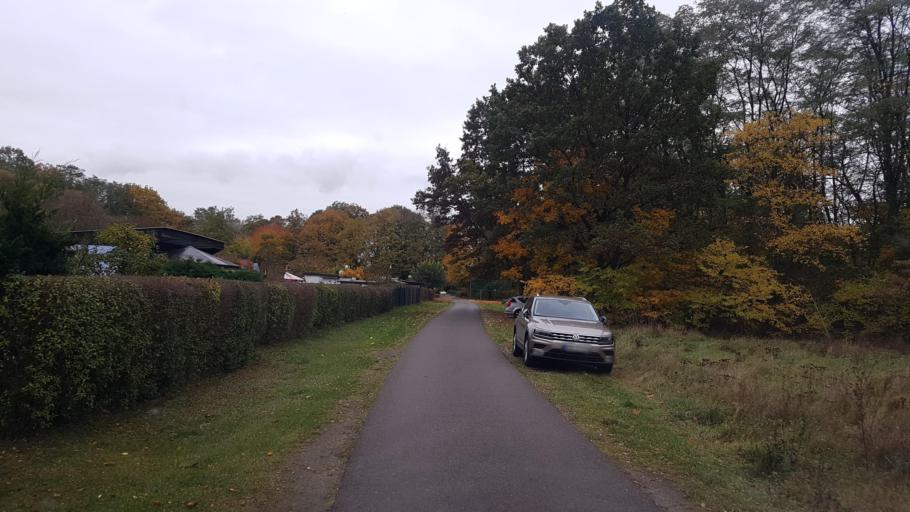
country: DE
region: Brandenburg
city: Spremberg
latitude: 51.5802
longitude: 14.3640
